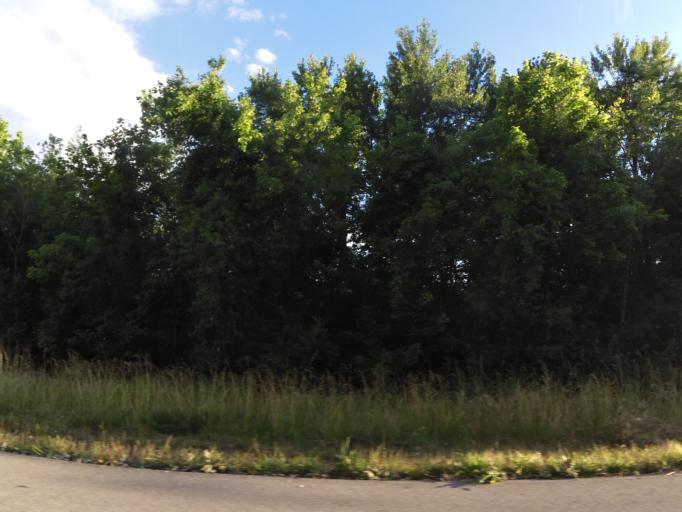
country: US
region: Missouri
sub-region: Jefferson County
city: Byrnes Mill
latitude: 38.4190
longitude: -90.5889
